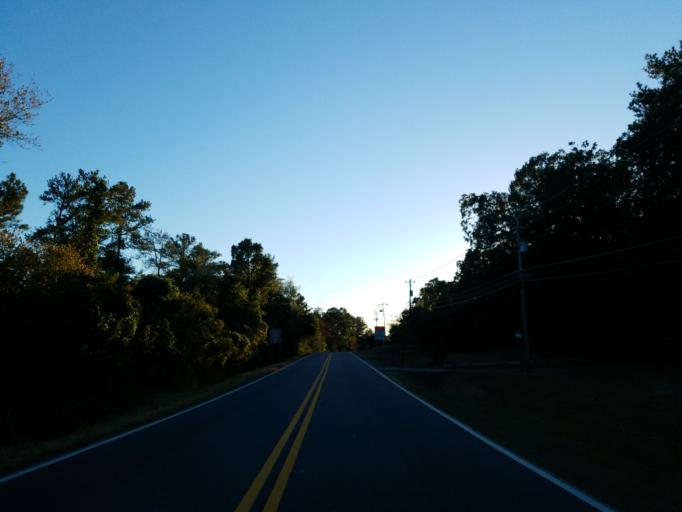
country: US
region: Georgia
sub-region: Forsyth County
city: Cumming
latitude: 34.2521
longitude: -84.1079
